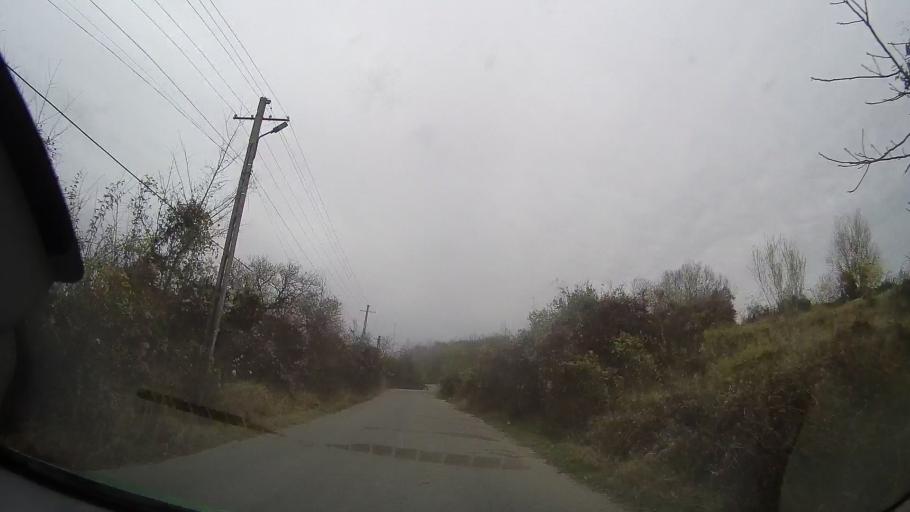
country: RO
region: Prahova
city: Mocesti
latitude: 45.0639
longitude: 26.2591
